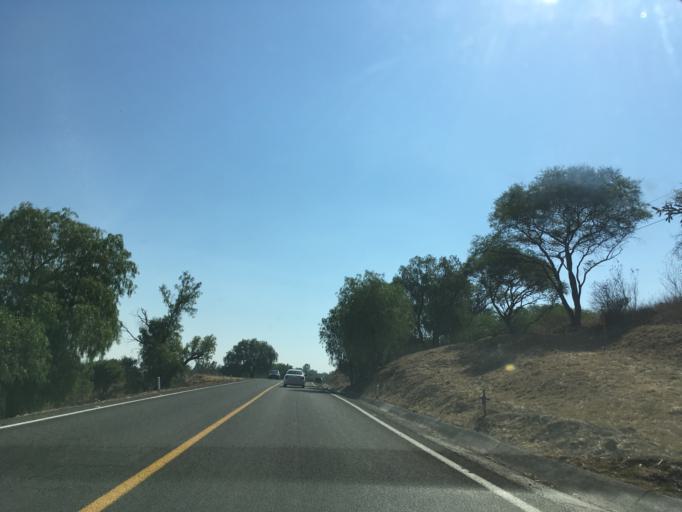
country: MX
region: Michoacan
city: Indaparapeo
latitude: 19.7816
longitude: -101.0041
